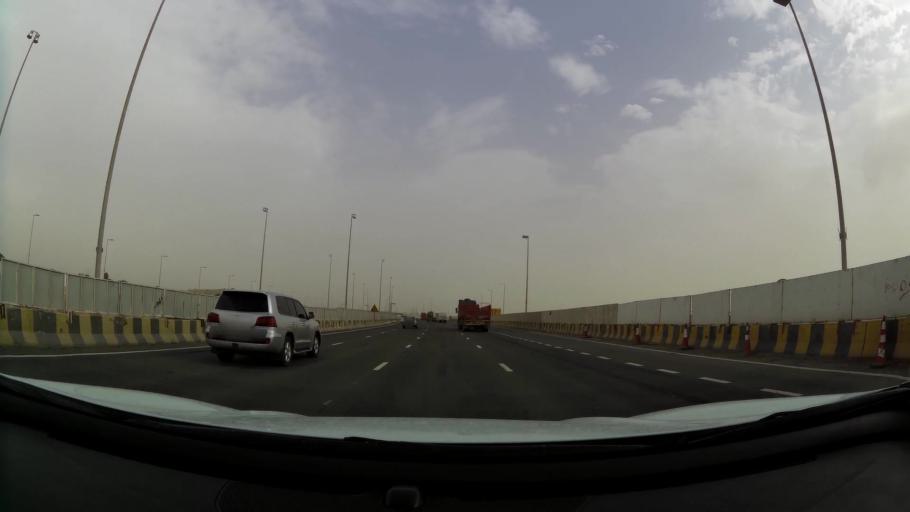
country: AE
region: Abu Dhabi
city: Abu Dhabi
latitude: 24.4584
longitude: 54.6269
